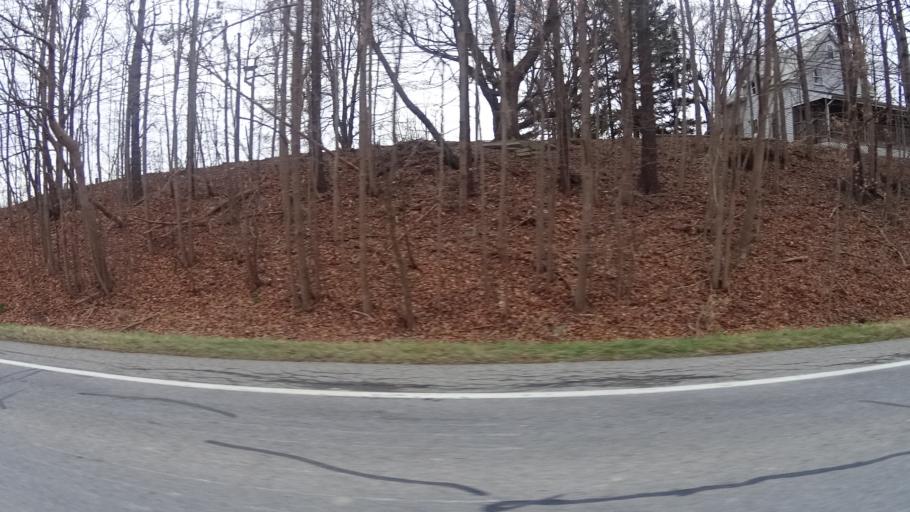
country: US
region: Ohio
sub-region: Lorain County
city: Camden
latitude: 41.1707
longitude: -82.3002
